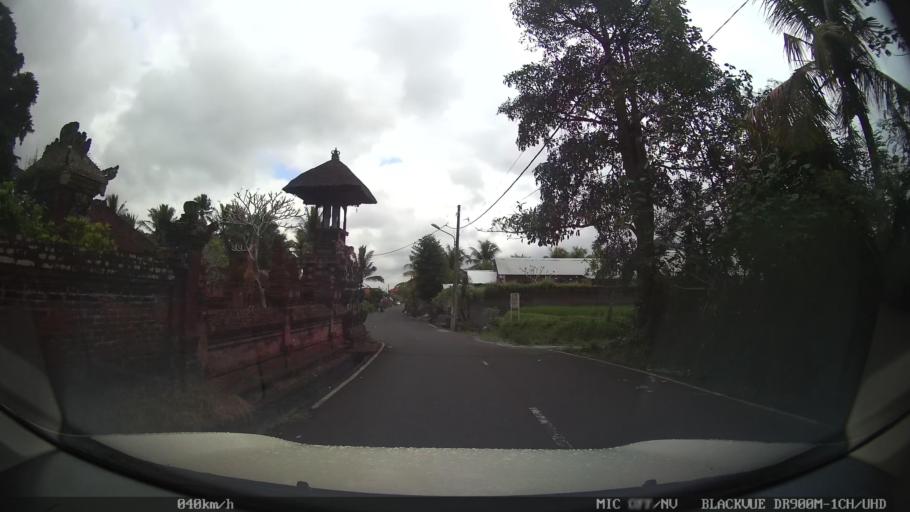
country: ID
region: Bali
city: Banjar Serangan
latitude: -8.5401
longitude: 115.1839
